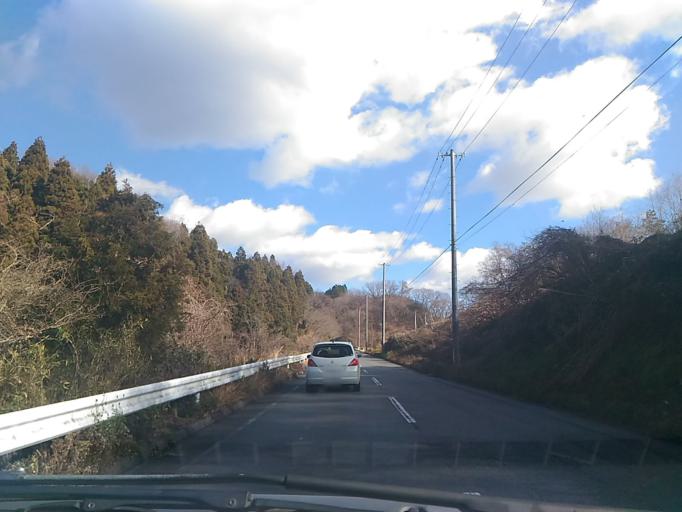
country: JP
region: Fukushima
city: Iwaki
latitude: 37.0048
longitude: 140.8174
